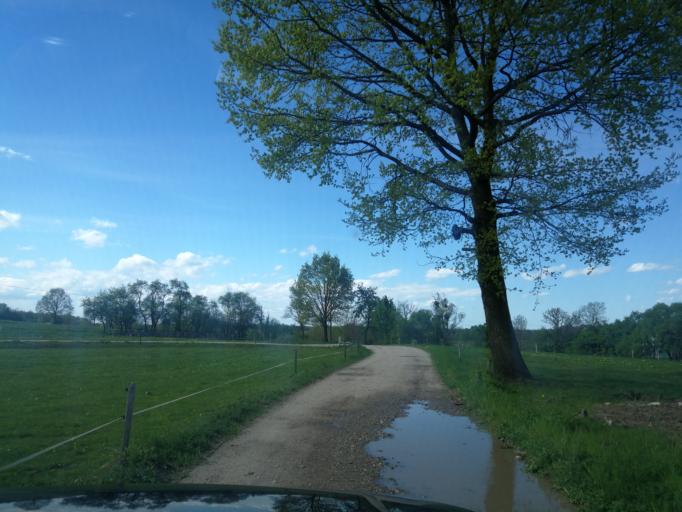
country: PL
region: Warmian-Masurian Voivodeship
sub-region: Powiat ilawski
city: Zalewo
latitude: 53.7610
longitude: 19.6749
